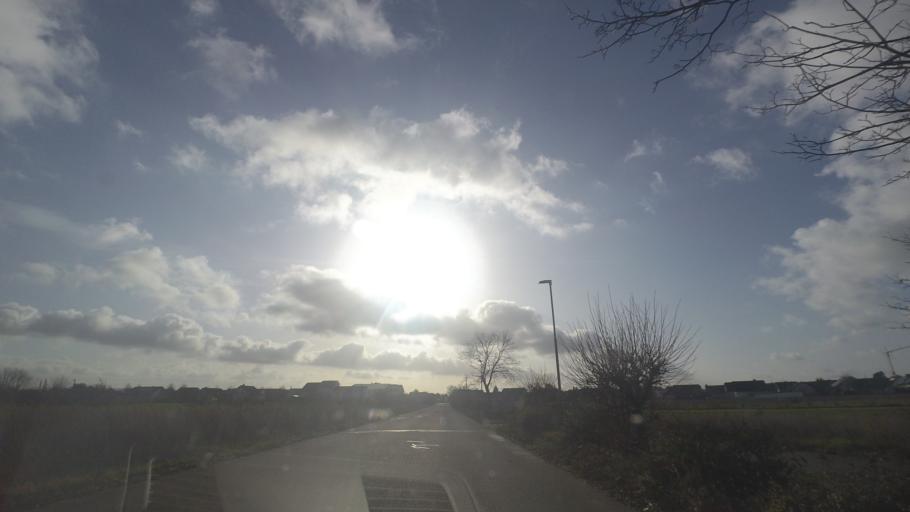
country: DE
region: Baden-Wuerttemberg
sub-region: Karlsruhe Region
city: Karlsdorf-Neuthard
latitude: 49.1209
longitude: 8.5108
